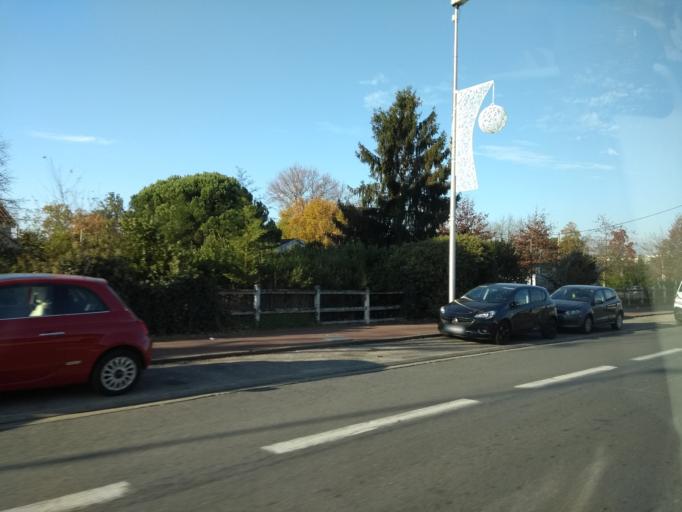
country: FR
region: Aquitaine
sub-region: Departement de la Gironde
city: Gradignan
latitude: 44.7771
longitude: -0.6107
